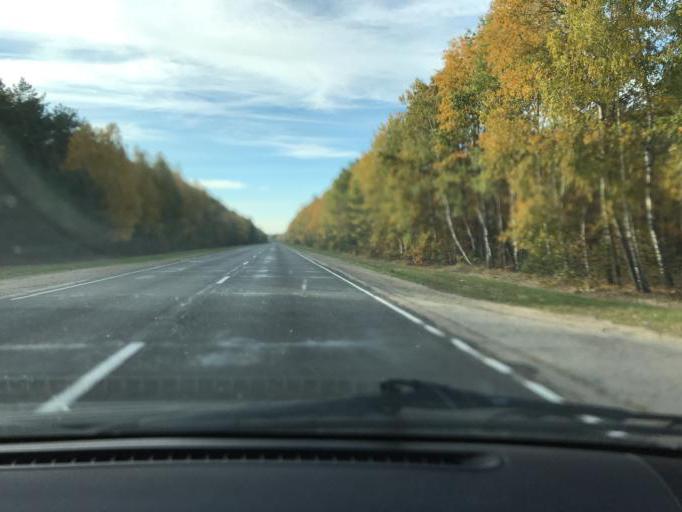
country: BY
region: Brest
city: Ivanava
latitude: 52.1561
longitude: 25.7765
